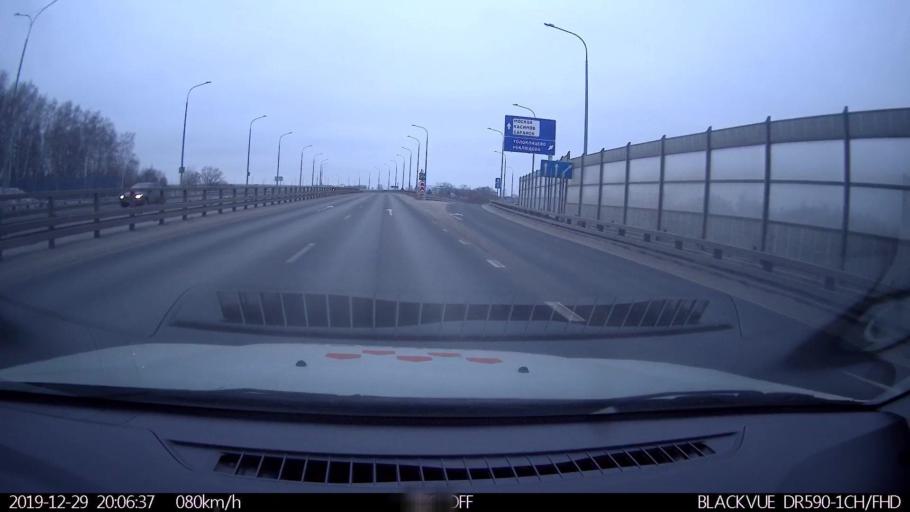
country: RU
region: Nizjnij Novgorod
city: Neklyudovo
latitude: 56.3968
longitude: 43.9990
